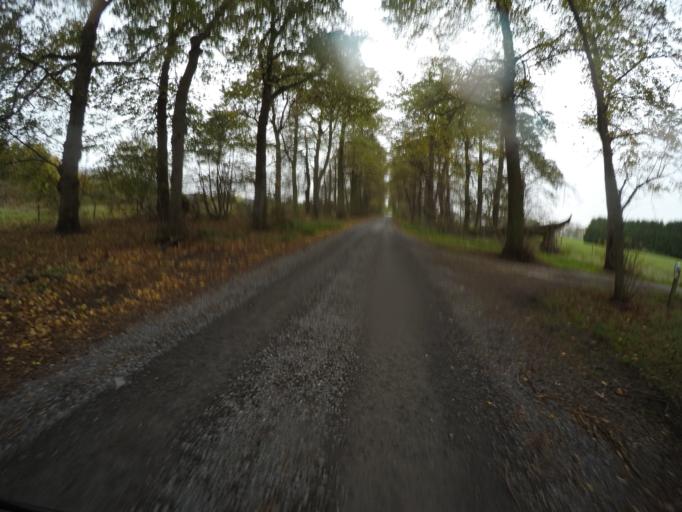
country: BE
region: Flanders
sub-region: Provincie Antwerpen
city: Borsbeek
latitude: 51.2244
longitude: 4.4907
